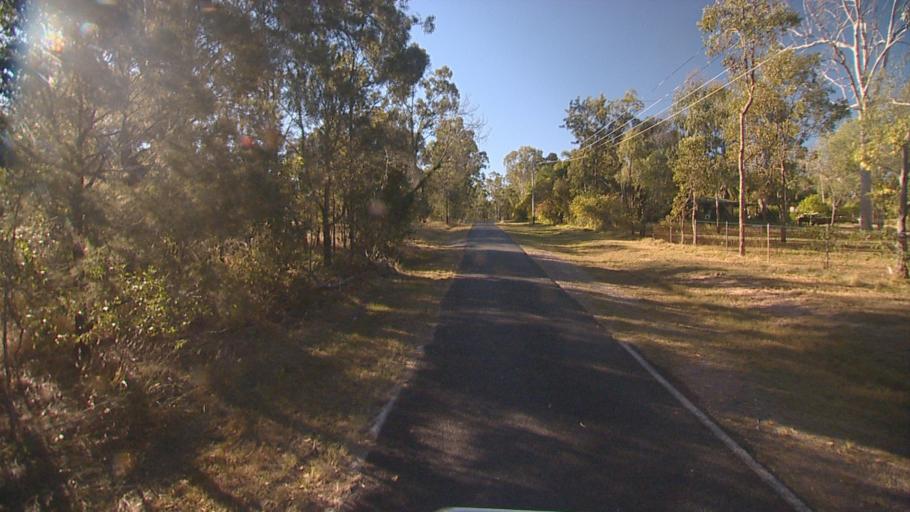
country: AU
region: Queensland
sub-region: Logan
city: North Maclean
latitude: -27.7549
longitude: 153.0052
